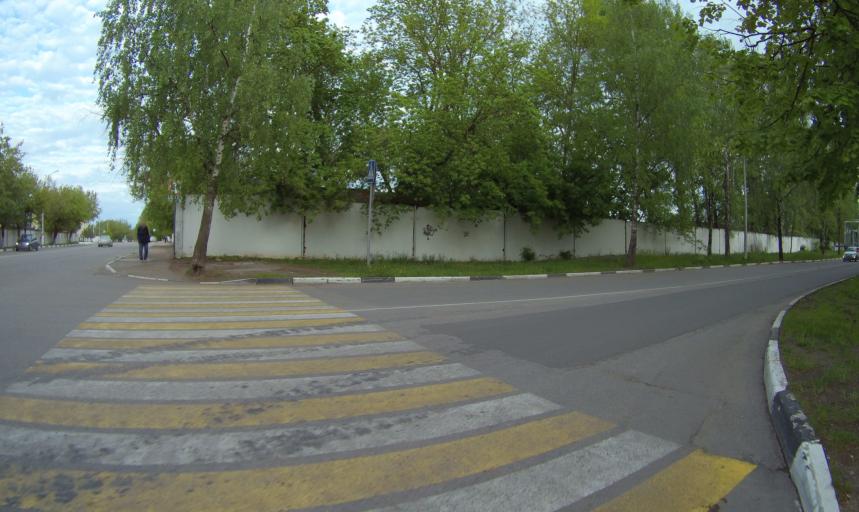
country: RU
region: Moskovskaya
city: Ramenskoye
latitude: 55.5705
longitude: 38.2464
